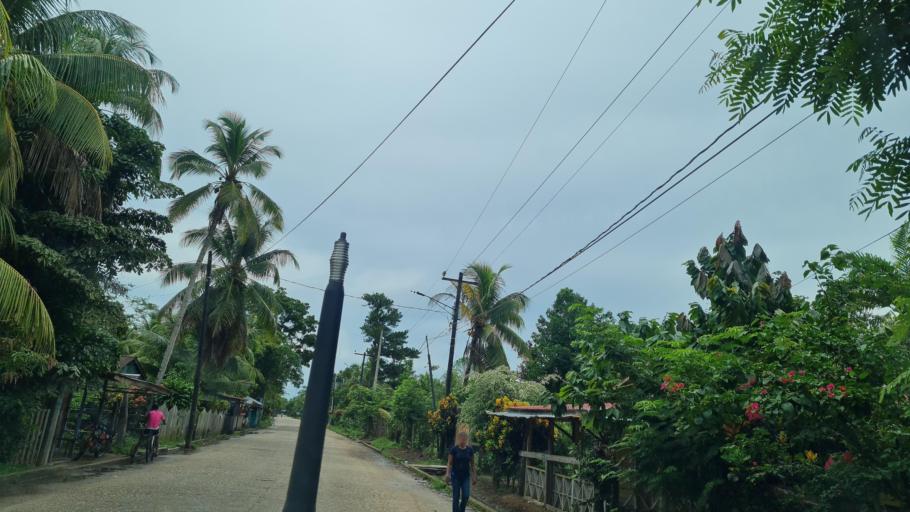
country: NI
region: Atlantico Norte (RAAN)
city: Waspam
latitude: 14.7336
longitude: -83.9690
